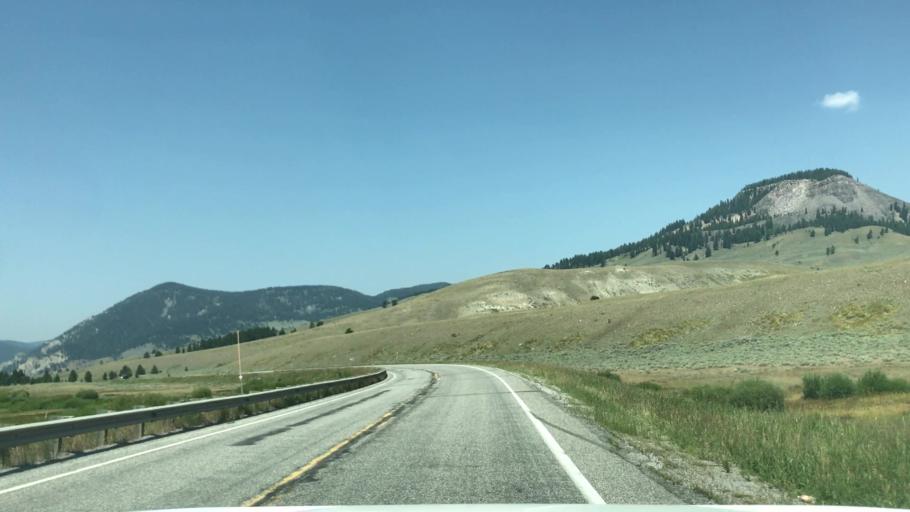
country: US
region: Montana
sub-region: Gallatin County
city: Big Sky
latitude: 45.0441
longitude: -111.1319
